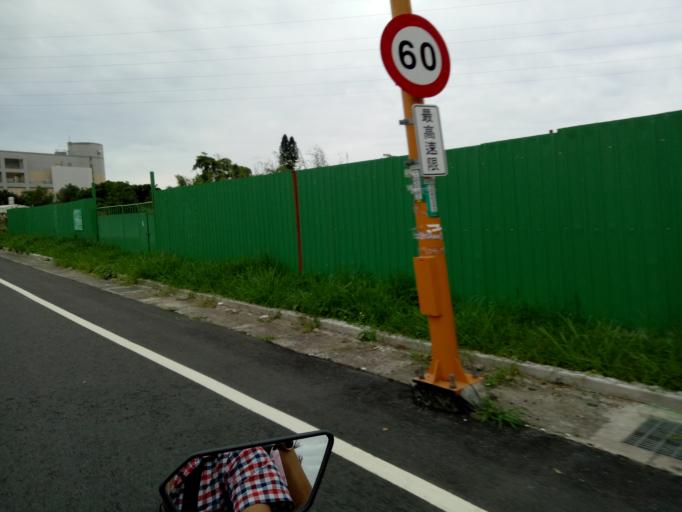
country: TW
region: Taiwan
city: Daxi
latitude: 24.8698
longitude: 121.2589
